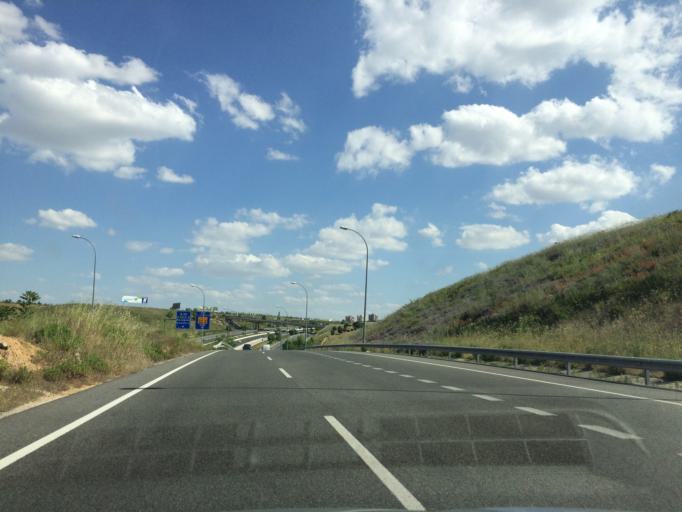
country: ES
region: Madrid
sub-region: Provincia de Madrid
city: Hortaleza
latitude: 40.4952
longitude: -3.6474
